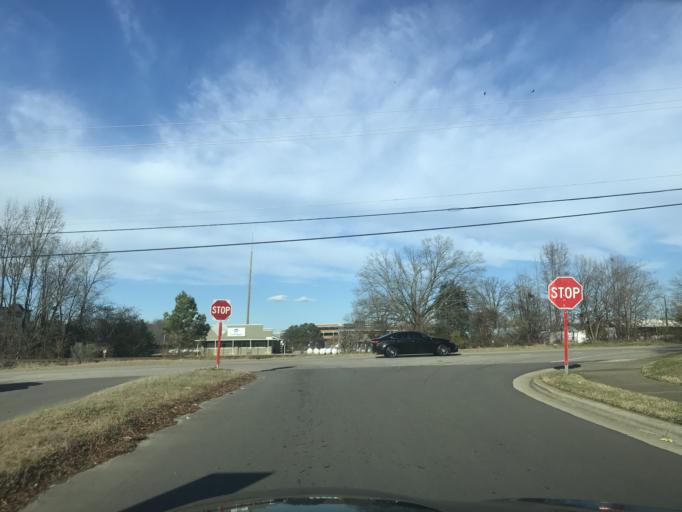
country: US
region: North Carolina
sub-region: Wake County
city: Cary
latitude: 35.7884
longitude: -78.7429
